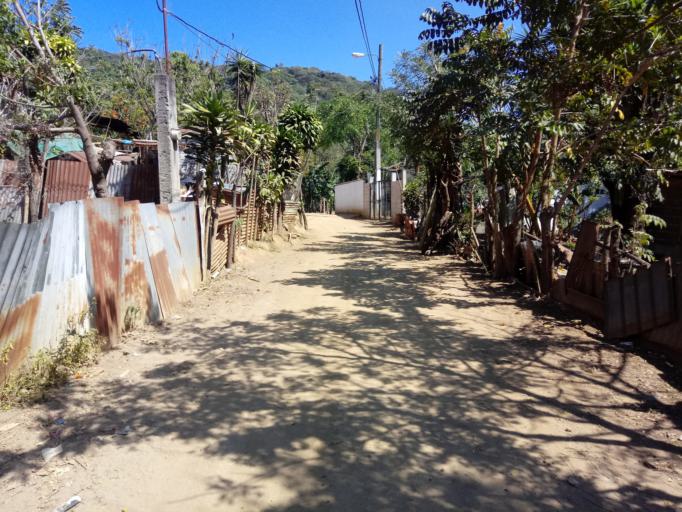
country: GT
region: Escuintla
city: San Vicente Pacaya
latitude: 14.4412
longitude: -90.6183
